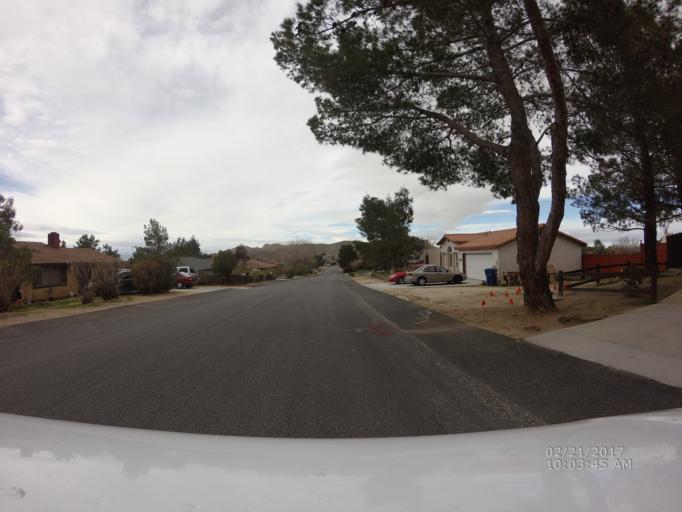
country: US
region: California
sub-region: Los Angeles County
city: Lake Los Angeles
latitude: 34.6018
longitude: -117.8196
